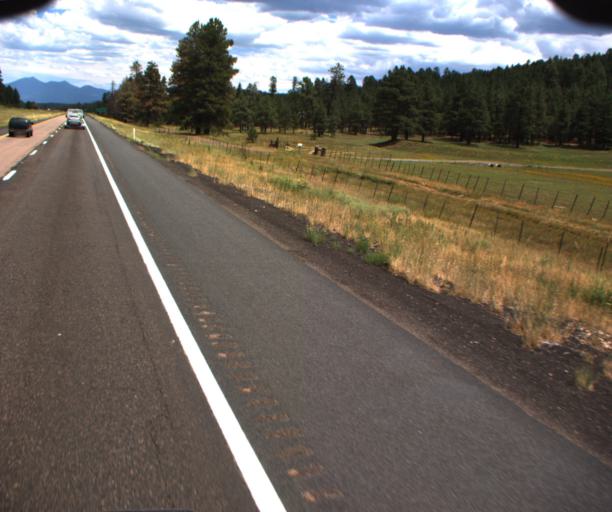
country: US
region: Arizona
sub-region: Coconino County
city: Mountainaire
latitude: 35.0101
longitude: -111.6851
